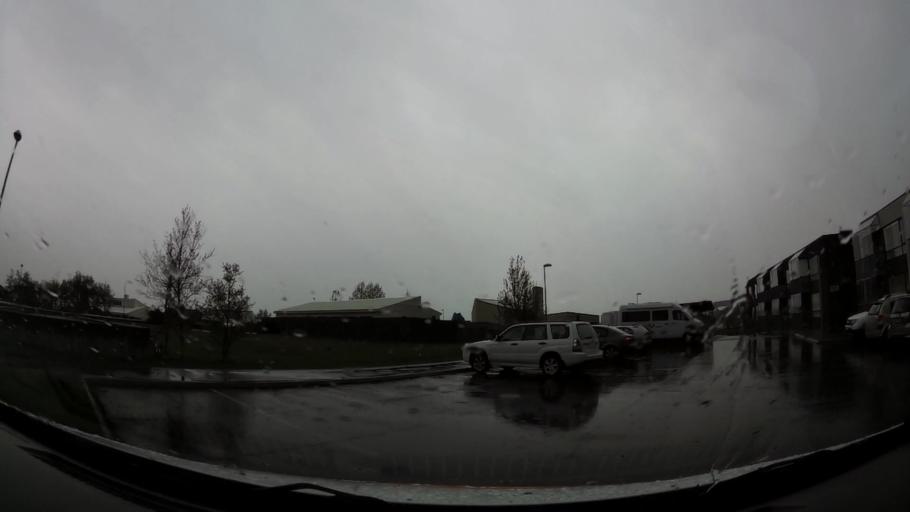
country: IS
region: Capital Region
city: Reykjavik
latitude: 64.1045
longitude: -21.8120
